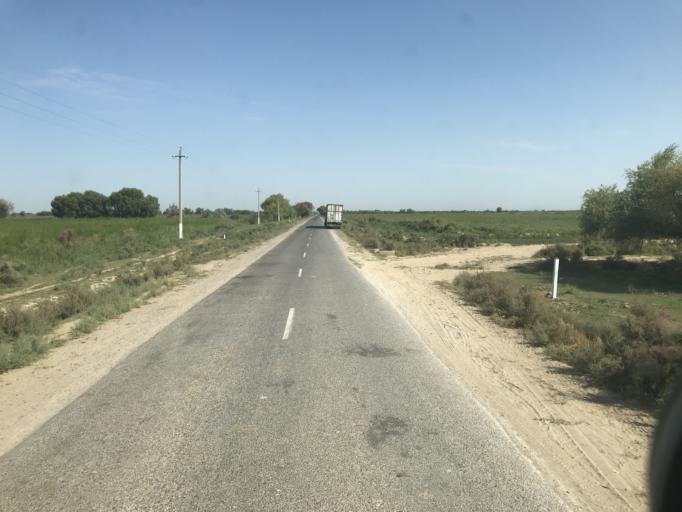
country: KZ
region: Ongtustik Qazaqstan
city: Myrzakent
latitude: 40.6685
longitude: 68.6332
